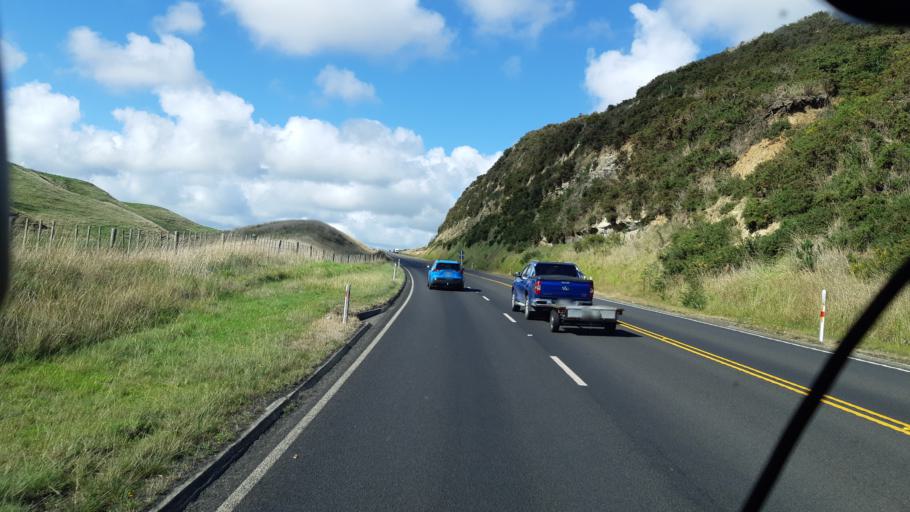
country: NZ
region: Manawatu-Wanganui
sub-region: Wanganui District
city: Wanganui
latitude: -40.0238
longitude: 175.1806
